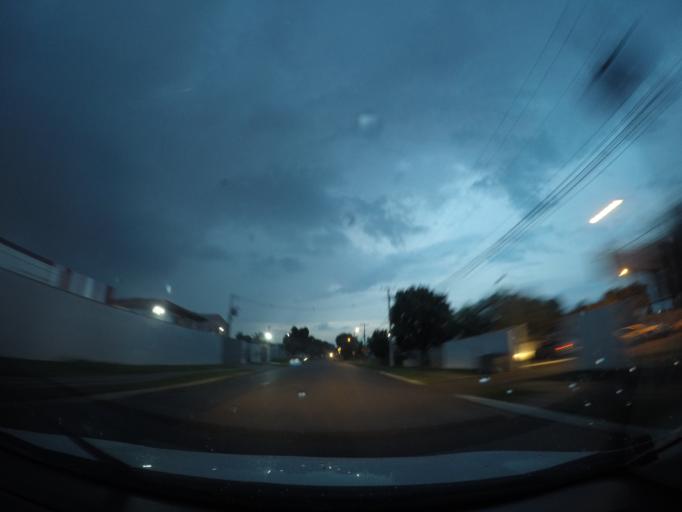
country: BR
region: Parana
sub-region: Sao Jose Dos Pinhais
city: Sao Jose dos Pinhais
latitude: -25.5171
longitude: -49.2259
